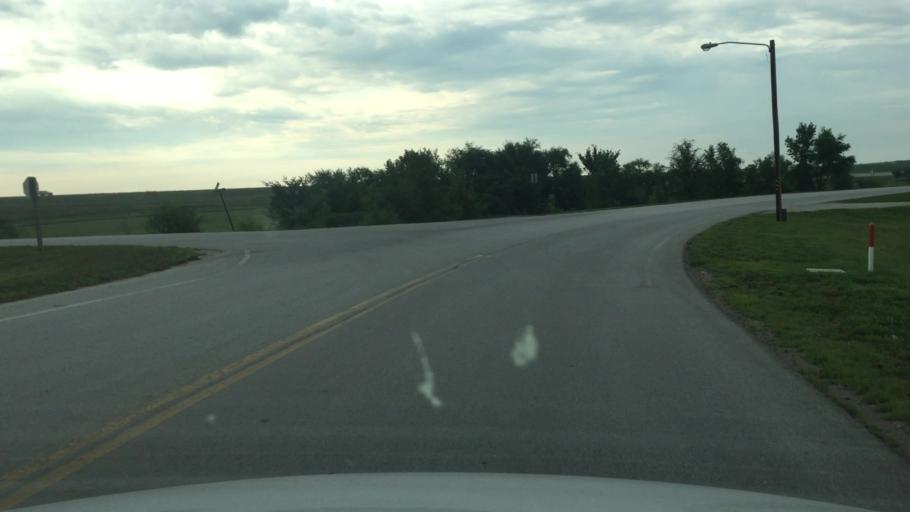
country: US
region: Kansas
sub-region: Nemaha County
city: Sabetha
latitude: 39.9028
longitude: -95.7856
